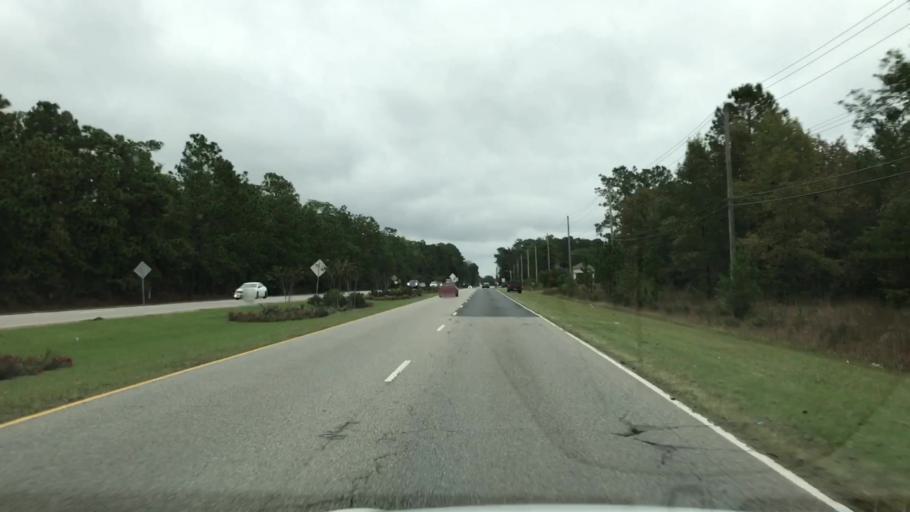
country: US
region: South Carolina
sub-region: Georgetown County
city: Georgetown
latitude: 33.3351
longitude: -79.3077
